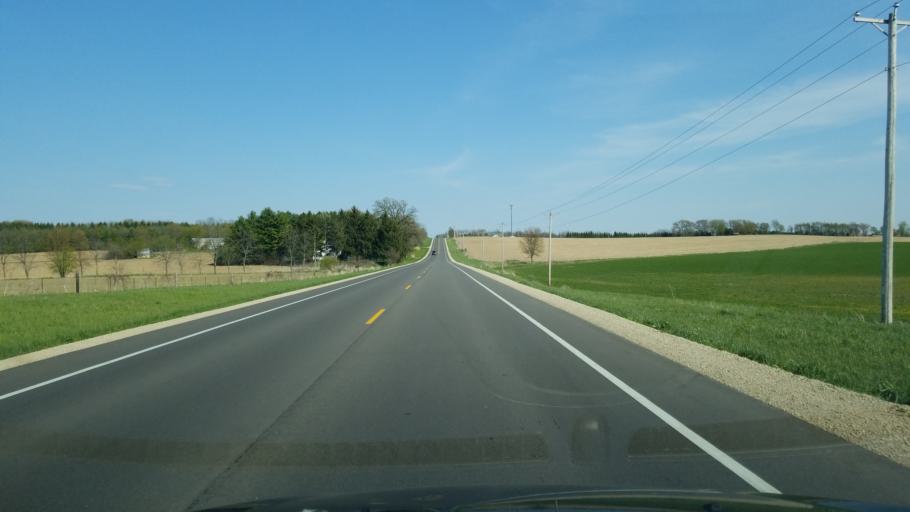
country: US
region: Wisconsin
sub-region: Dane County
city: Fitchburg
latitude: 42.9555
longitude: -89.4688
